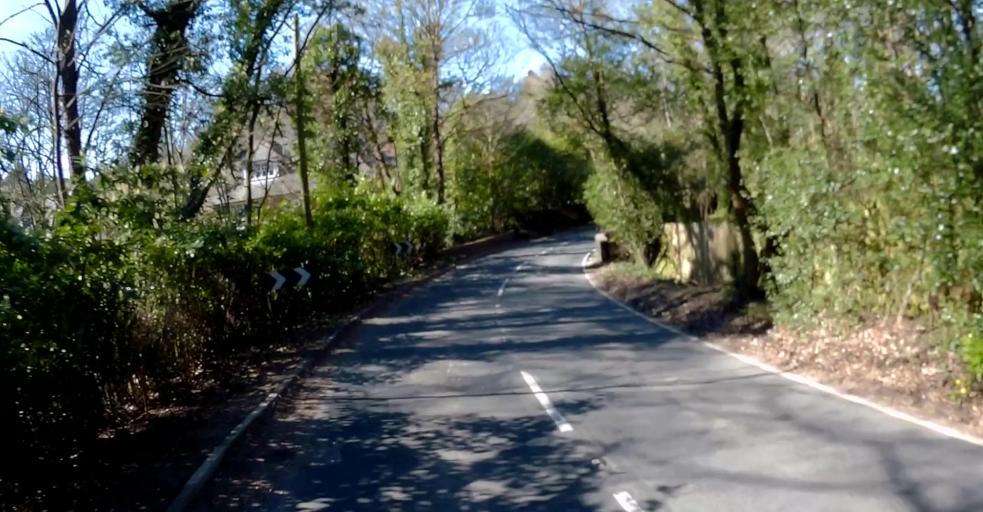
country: GB
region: England
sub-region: Surrey
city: Farnham
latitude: 51.2016
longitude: -0.7773
